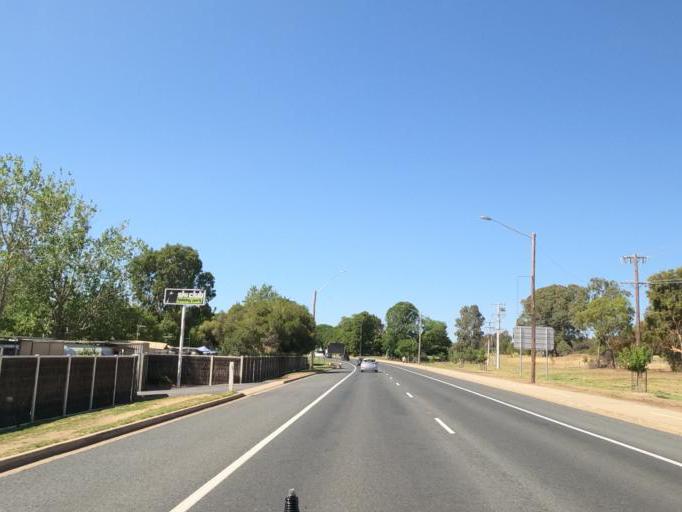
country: AU
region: New South Wales
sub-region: Corowa Shire
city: Mulwala
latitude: -35.9970
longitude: 146.0008
